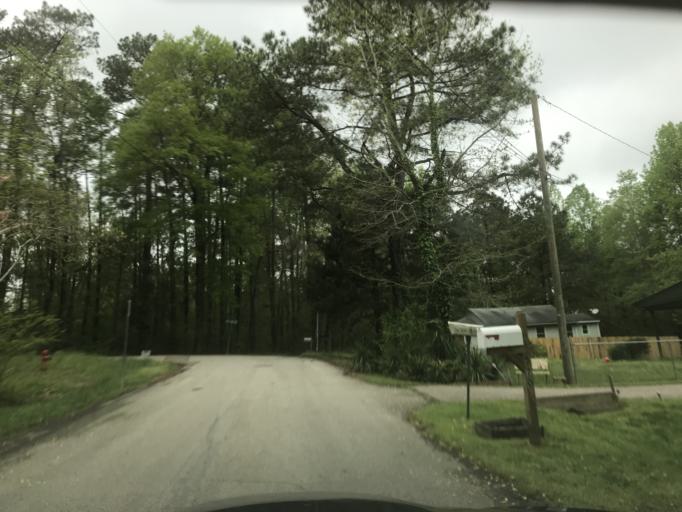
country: US
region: North Carolina
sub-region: Wake County
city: Raleigh
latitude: 35.7498
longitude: -78.6545
